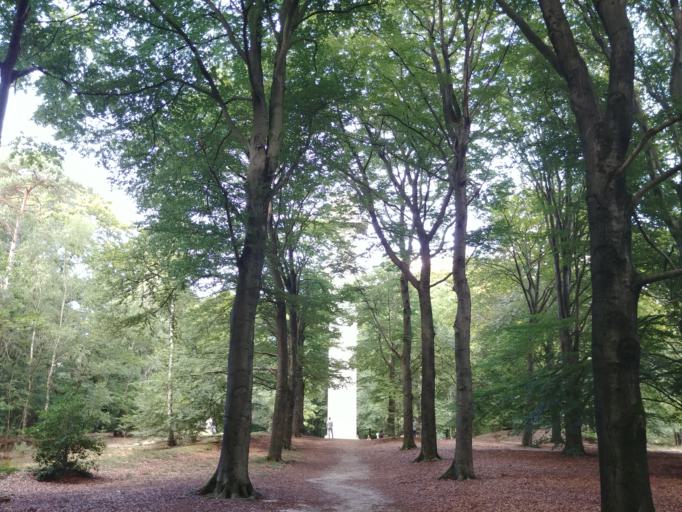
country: NL
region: Utrecht
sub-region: Gemeente Utrechtse Heuvelrug
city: Doorn
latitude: 52.0410
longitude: 5.3652
